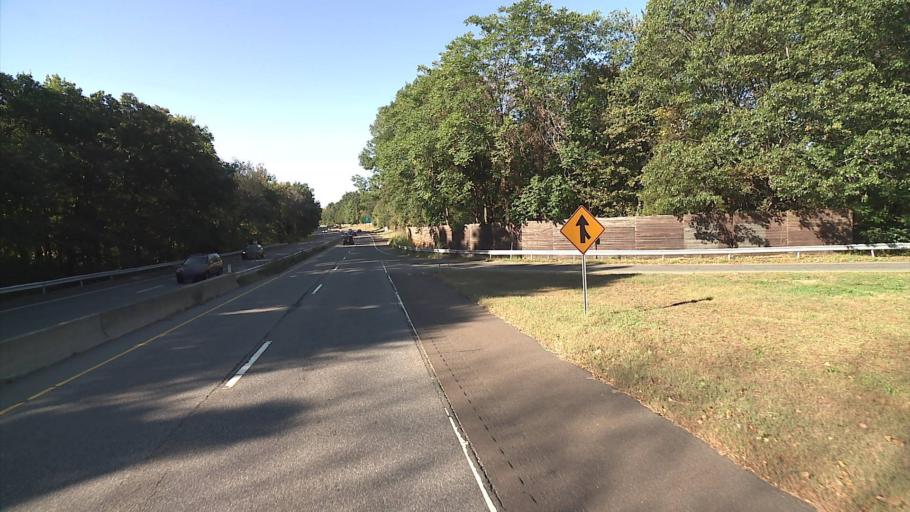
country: US
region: Connecticut
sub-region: New Haven County
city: Hamden
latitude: 41.3782
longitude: -72.9050
